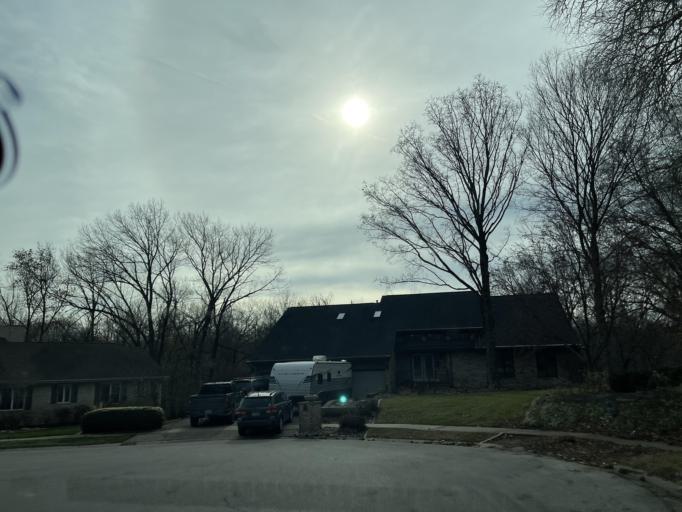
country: US
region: Illinois
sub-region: Sangamon County
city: Leland Grove
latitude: 39.8086
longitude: -89.7235
